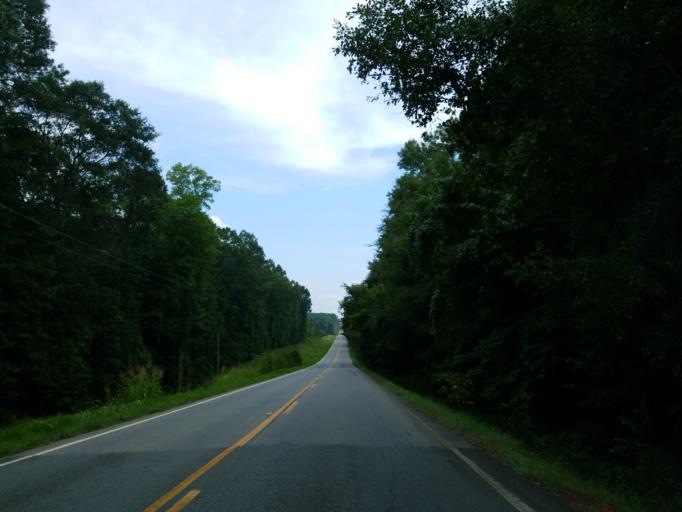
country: US
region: Georgia
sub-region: Dooly County
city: Unadilla
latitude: 32.3280
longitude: -83.7358
